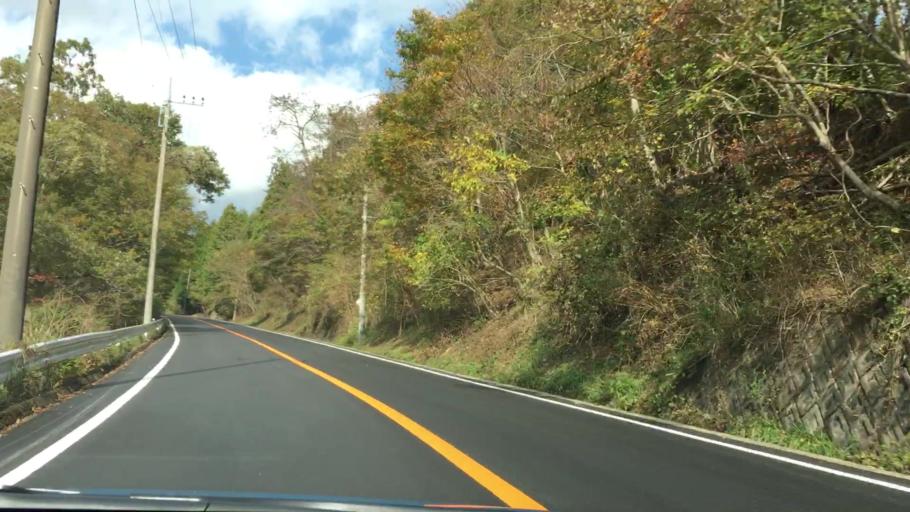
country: JP
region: Shizuoka
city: Gotemba
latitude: 35.3791
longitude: 138.9441
